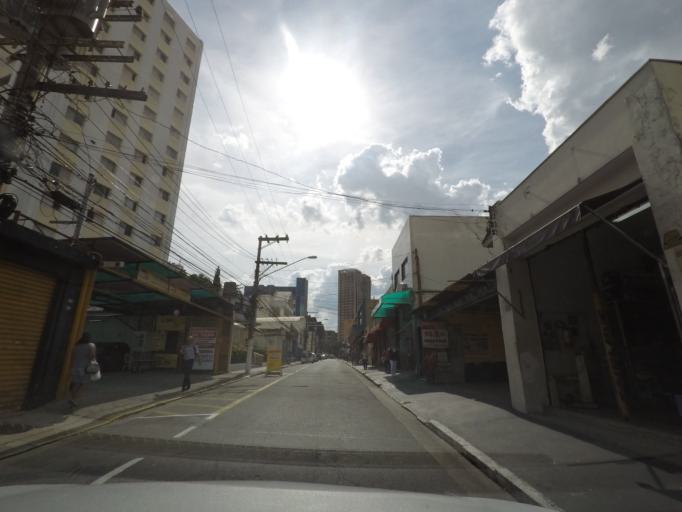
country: BR
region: Sao Paulo
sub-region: Diadema
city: Diadema
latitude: -23.6531
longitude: -46.7031
